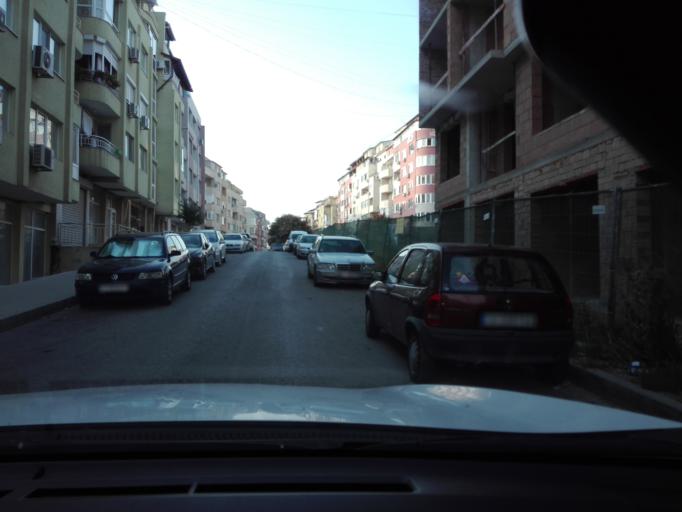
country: BG
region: Burgas
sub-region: Obshtina Burgas
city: Burgas
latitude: 42.4617
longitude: 27.4126
